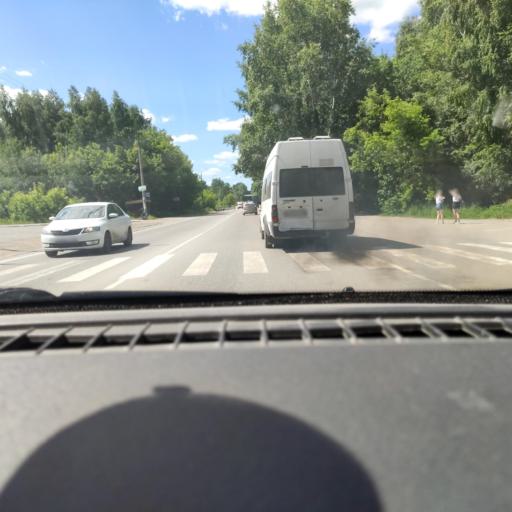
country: RU
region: Perm
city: Krasnokamsk
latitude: 58.0763
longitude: 55.7255
